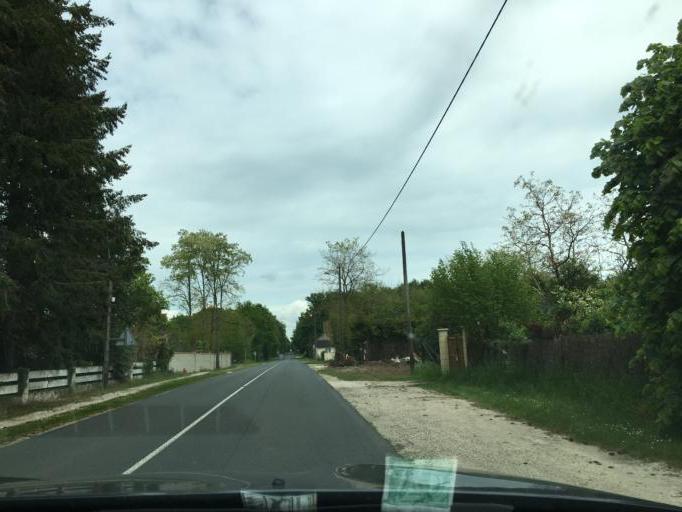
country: FR
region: Centre
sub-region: Departement du Loir-et-Cher
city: Dhuizon
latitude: 47.6637
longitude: 1.6694
